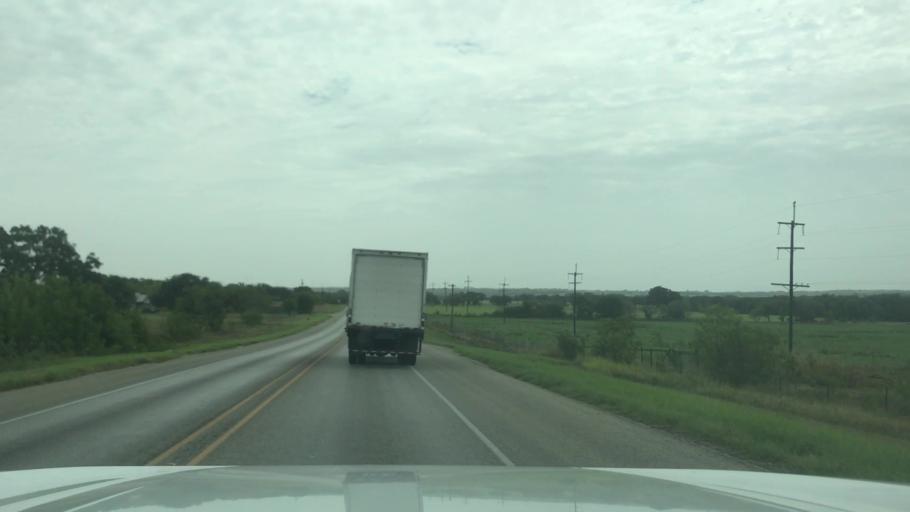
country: US
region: Texas
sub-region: Comanche County
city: De Leon
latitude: 32.0999
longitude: -98.4720
